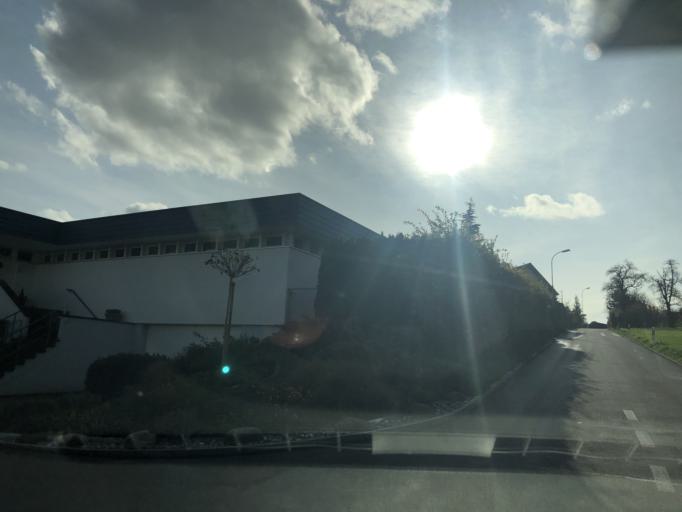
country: CH
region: Aargau
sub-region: Bezirk Baden
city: Obersiggenthal
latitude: 47.4752
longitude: 8.2838
